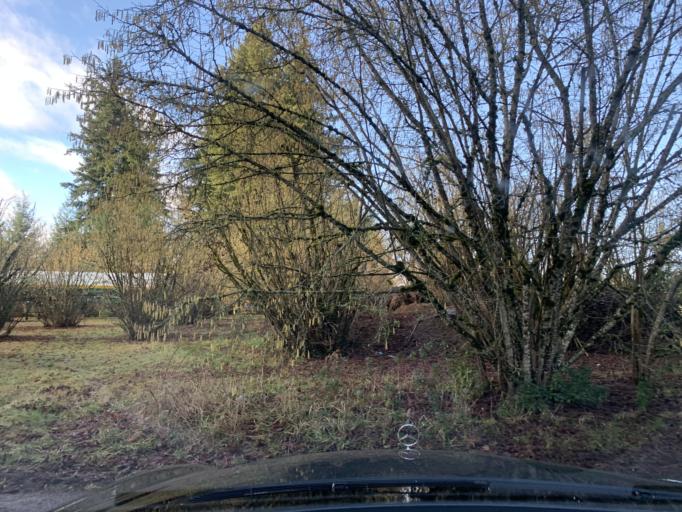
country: US
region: Washington
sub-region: Clark County
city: Brush Prairie
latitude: 45.7092
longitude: -122.5616
